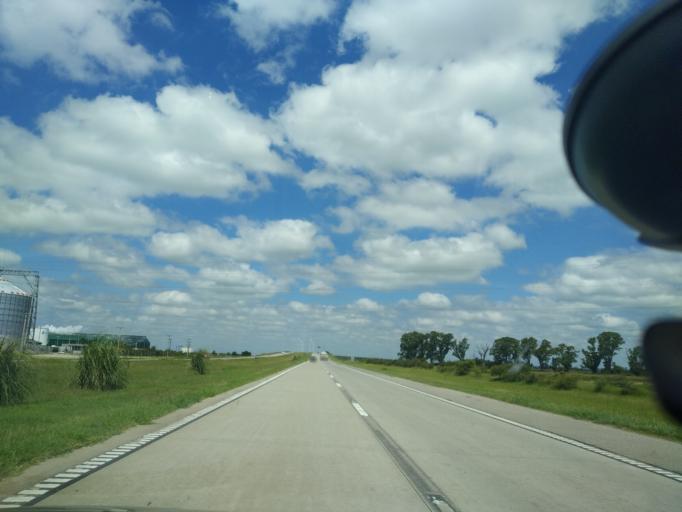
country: AR
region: Cordoba
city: Villa Maria
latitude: -32.4160
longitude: -63.1645
